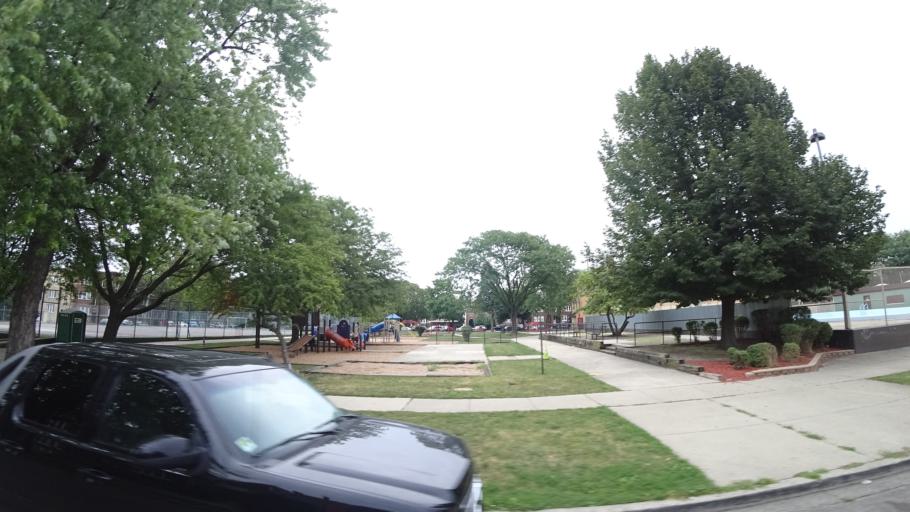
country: US
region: Illinois
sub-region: Cook County
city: Cicero
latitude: 41.8561
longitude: -87.7530
